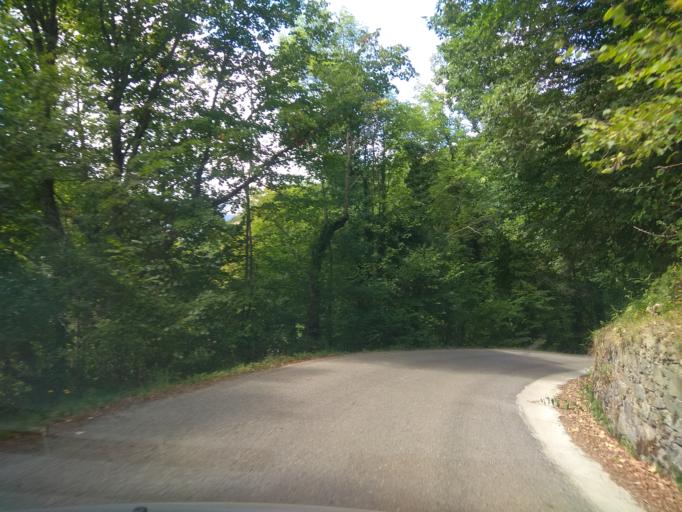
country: ES
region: Catalonia
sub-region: Provincia de Lleida
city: Vielha
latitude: 42.7281
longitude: 0.7300
